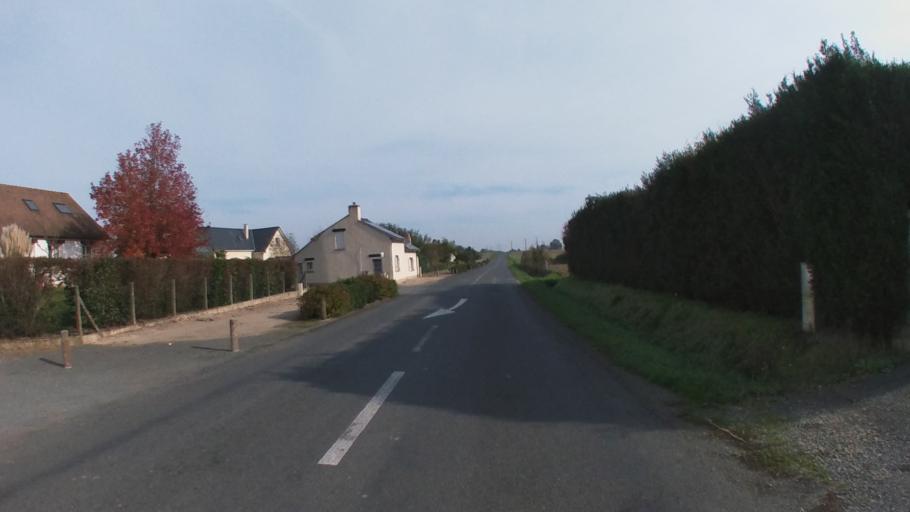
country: FR
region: Pays de la Loire
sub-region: Departement de la Sarthe
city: Juigne-sur-Sarthe
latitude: 47.8680
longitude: -0.2677
